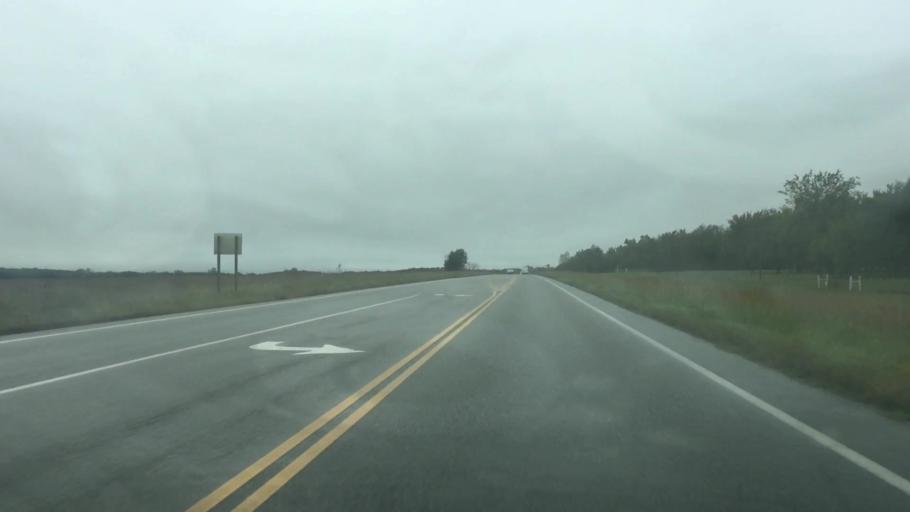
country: US
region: Kansas
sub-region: Anderson County
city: Garnett
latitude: 38.2653
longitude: -95.2419
